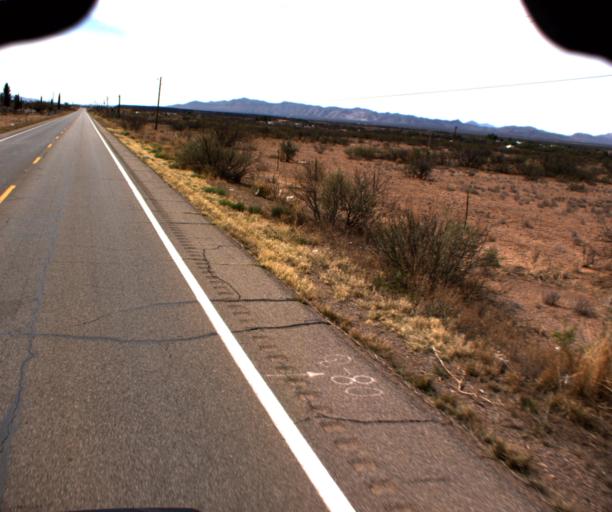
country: US
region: Arizona
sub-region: Cochise County
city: Pirtleville
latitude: 31.3679
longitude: -109.5794
